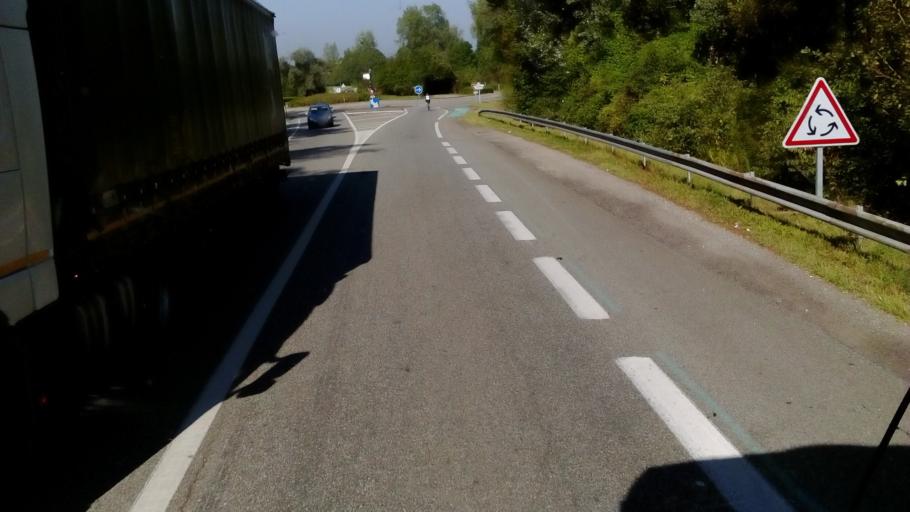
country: FR
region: Alsace
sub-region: Departement du Bas-Rhin
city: Gambsheim
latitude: 48.6889
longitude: 7.9073
